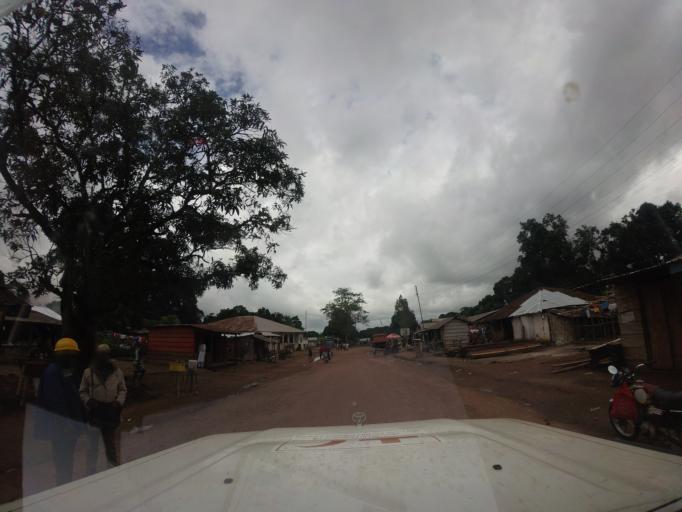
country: SL
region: Northern Province
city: Kukuna
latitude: 9.2890
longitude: -12.6734
